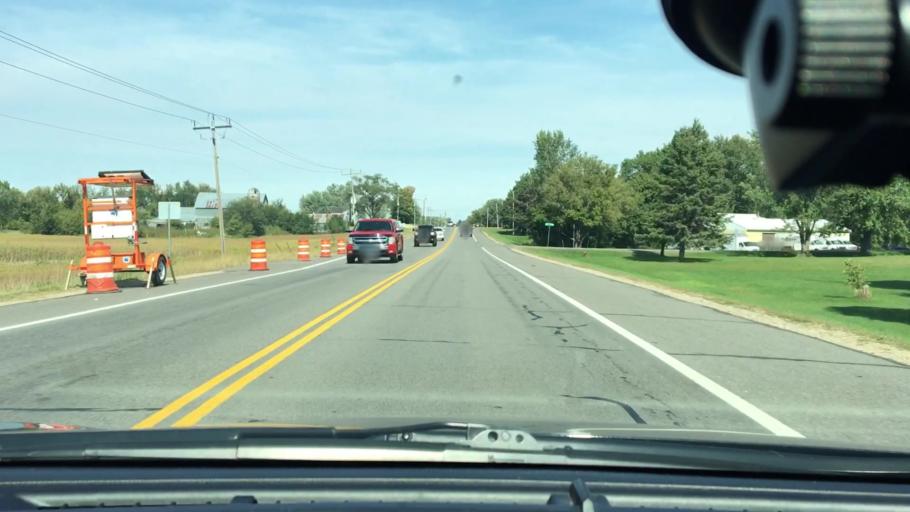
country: US
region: Minnesota
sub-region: Wright County
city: Saint Michael
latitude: 45.1894
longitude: -93.6652
